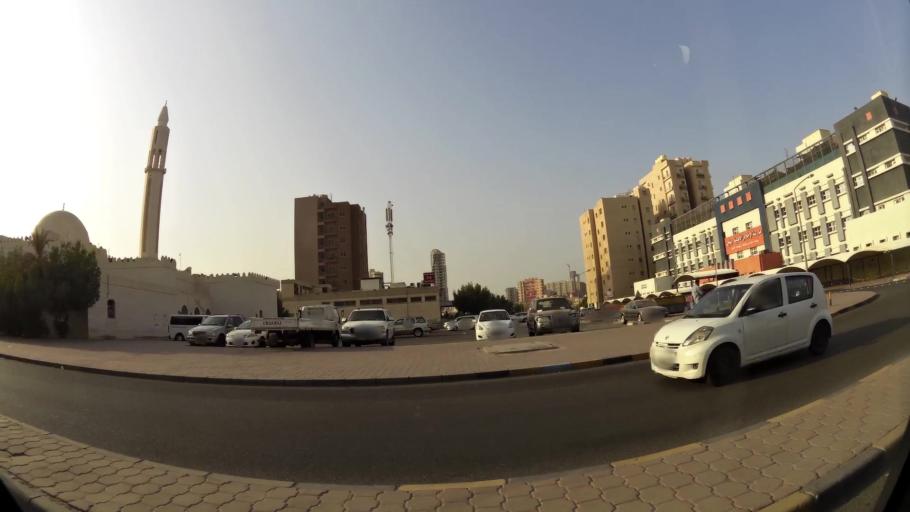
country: KW
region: Muhafazat Hawalli
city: Hawalli
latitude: 29.3279
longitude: 48.0489
